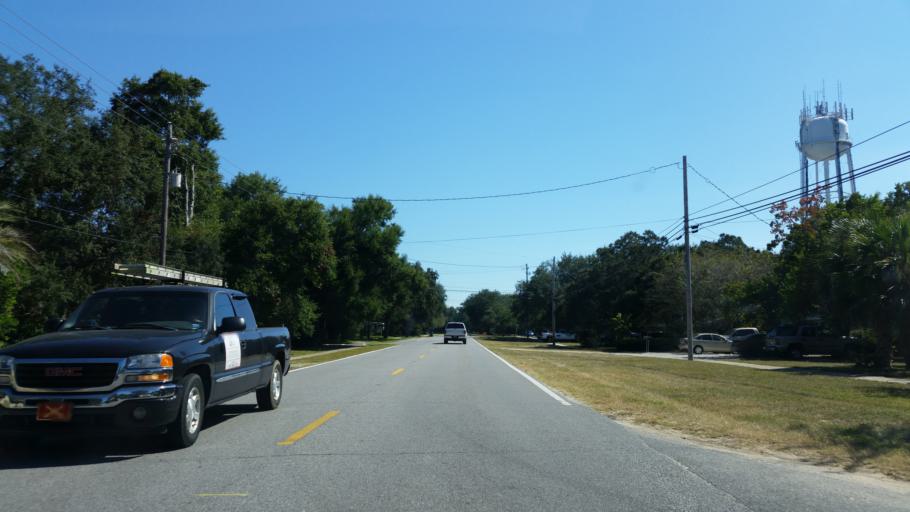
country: US
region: Florida
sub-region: Santa Rosa County
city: Gulf Breeze
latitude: 30.3606
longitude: -87.1839
